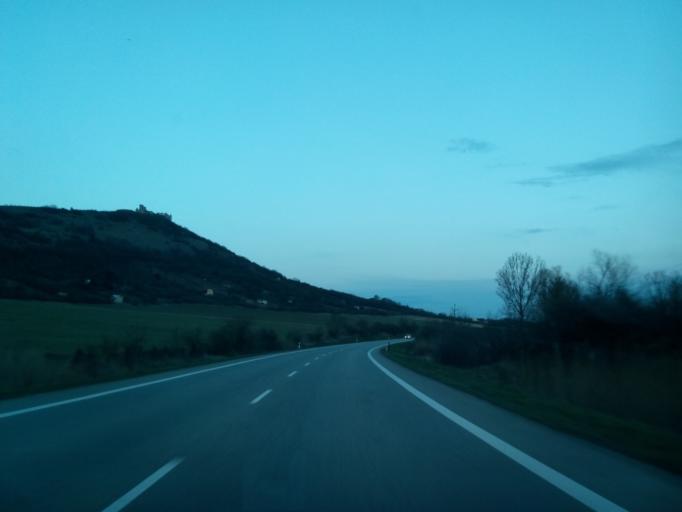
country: SK
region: Kosicky
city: Medzev
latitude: 48.6101
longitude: 20.8616
